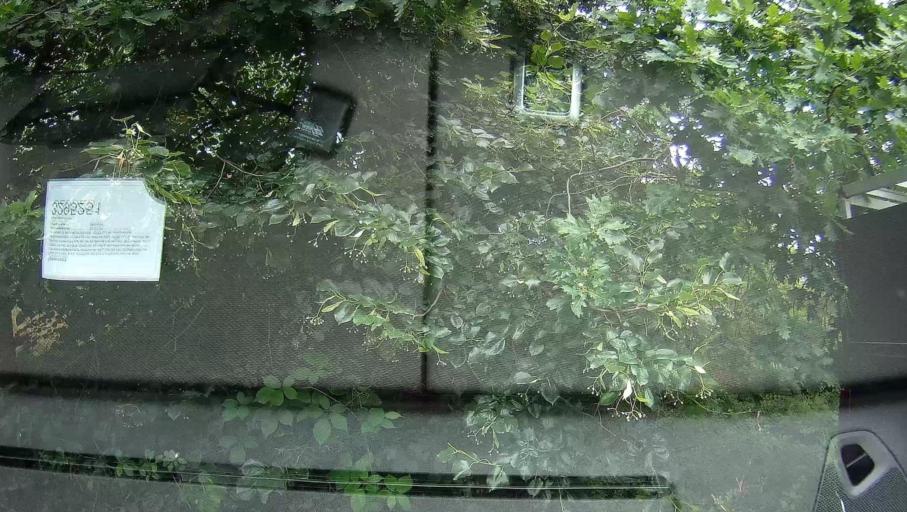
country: BE
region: Flanders
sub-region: Provincie Antwerpen
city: Balen
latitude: 51.2163
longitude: 5.1906
